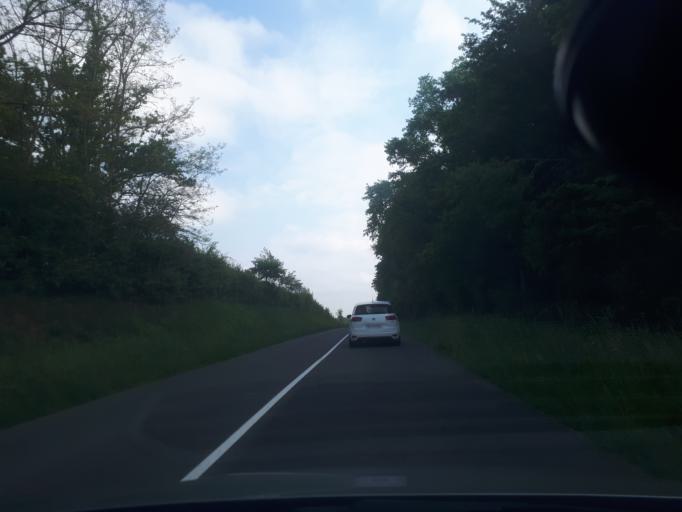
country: FR
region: Auvergne
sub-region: Departement de l'Allier
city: Dompierre-sur-Besbre
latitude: 46.4288
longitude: 3.6200
